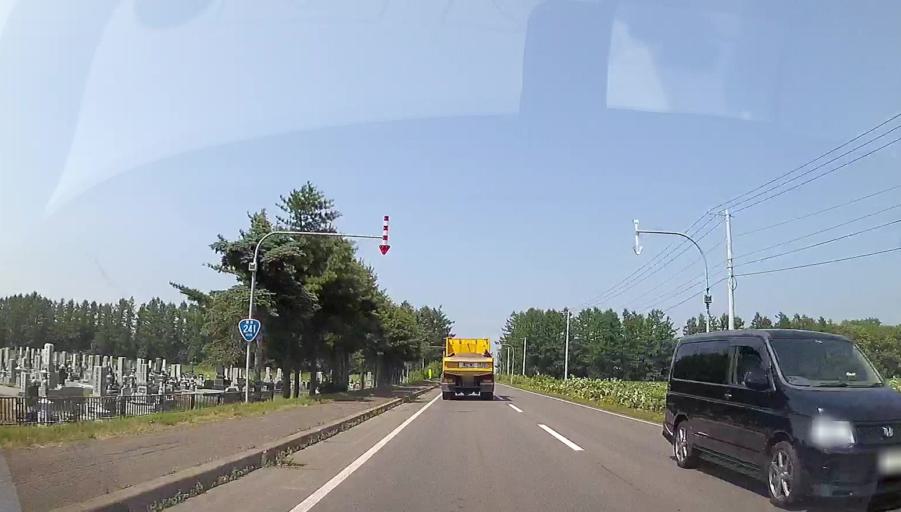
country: JP
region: Hokkaido
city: Otofuke
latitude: 43.1230
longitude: 143.2355
